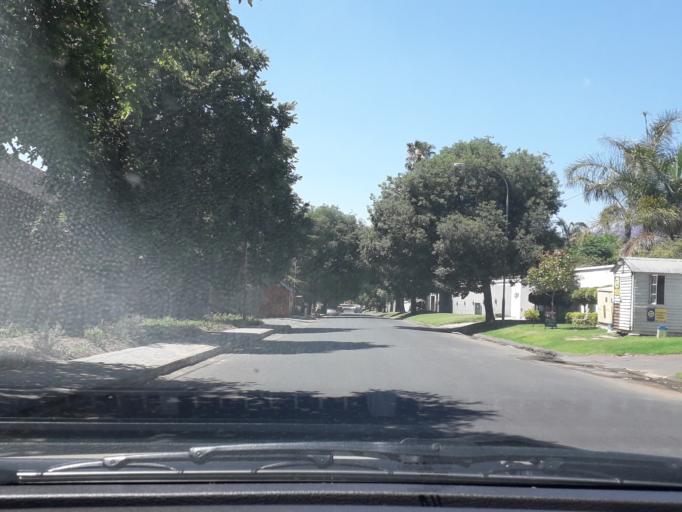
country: ZA
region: Gauteng
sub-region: City of Johannesburg Metropolitan Municipality
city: Johannesburg
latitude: -26.1519
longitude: 28.0691
